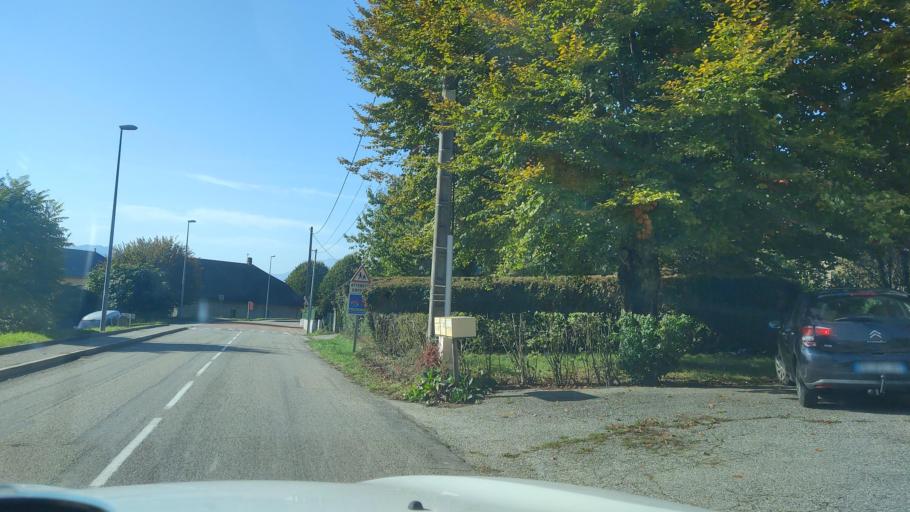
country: FR
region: Rhone-Alpes
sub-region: Departement de la Savoie
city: Coise-Saint-Jean-Pied-Gauthier
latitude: 45.5703
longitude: 6.1596
